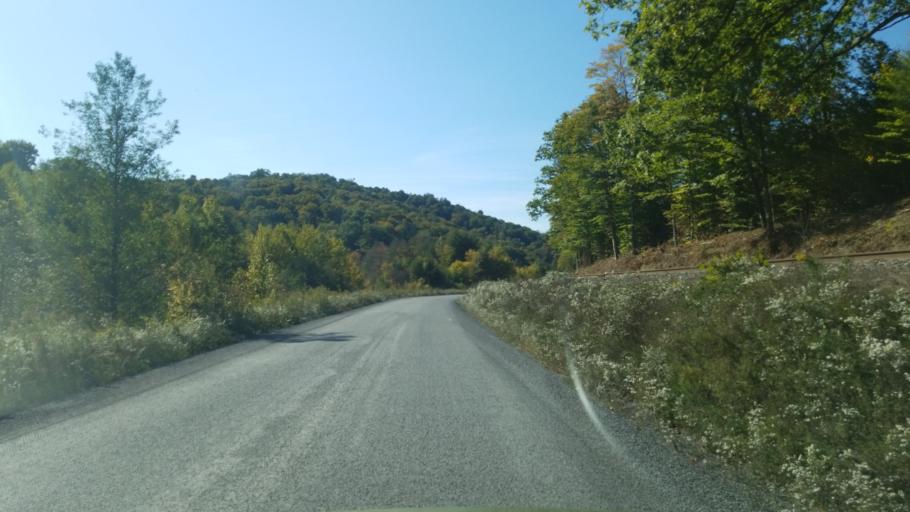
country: US
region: Pennsylvania
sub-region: Clearfield County
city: Treasure Lake
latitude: 41.2013
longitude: -78.5570
